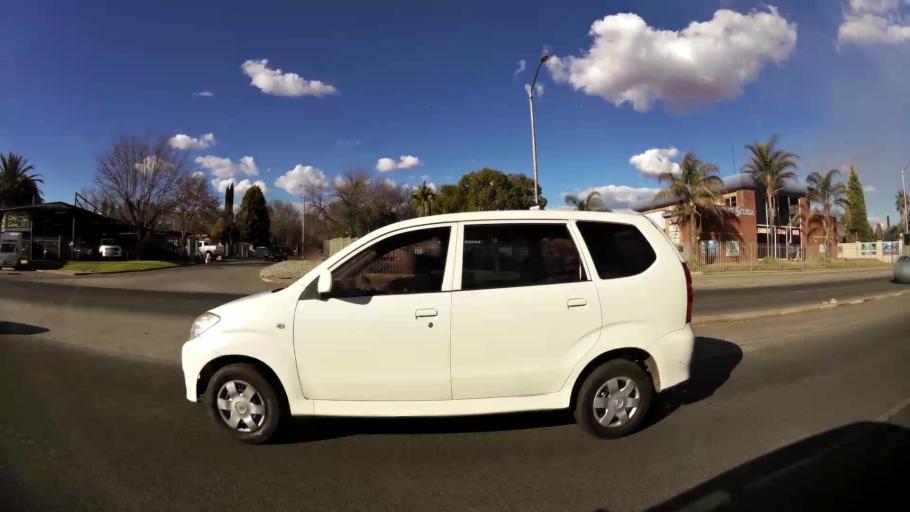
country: ZA
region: North-West
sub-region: Dr Kenneth Kaunda District Municipality
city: Klerksdorp
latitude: -26.8531
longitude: 26.6643
